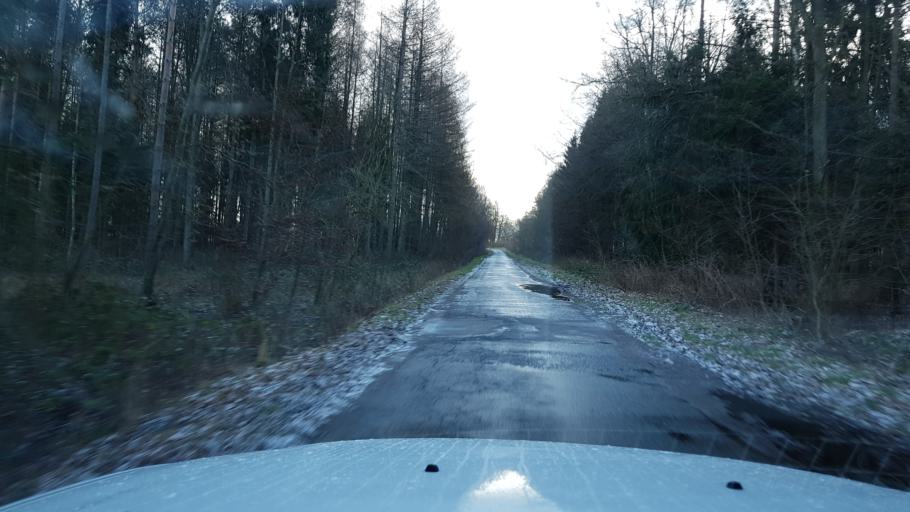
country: PL
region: West Pomeranian Voivodeship
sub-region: Powiat gryficki
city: Trzebiatow
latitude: 54.0416
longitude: 15.3397
